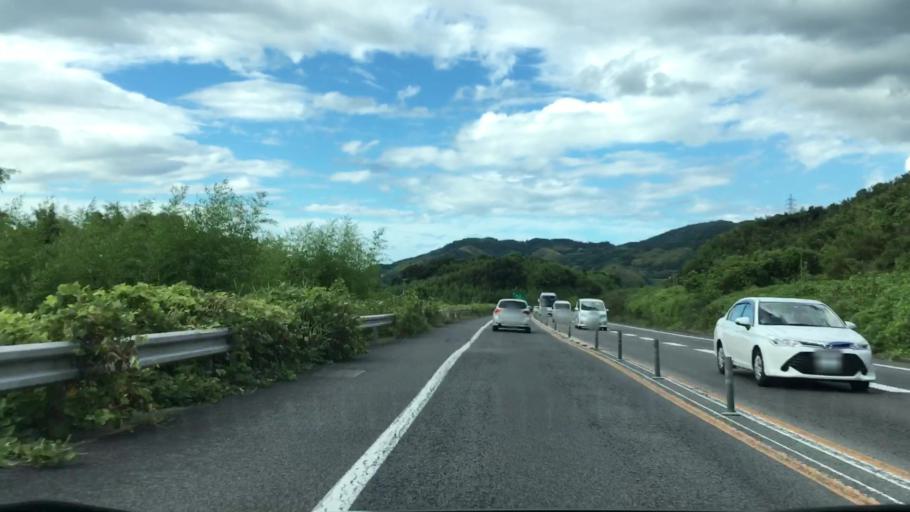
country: JP
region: Saga Prefecture
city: Karatsu
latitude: 33.4352
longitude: 130.0481
